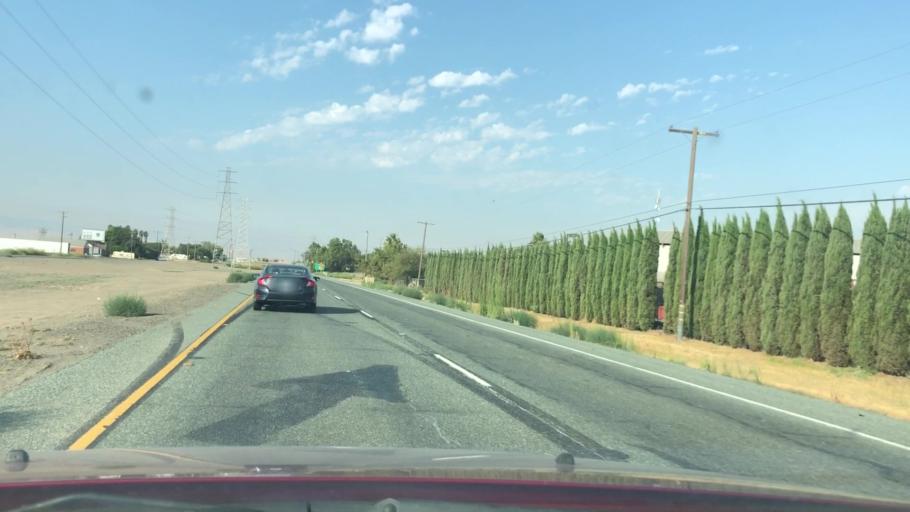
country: US
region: California
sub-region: San Joaquin County
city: Tracy
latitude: 37.7561
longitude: -121.3483
